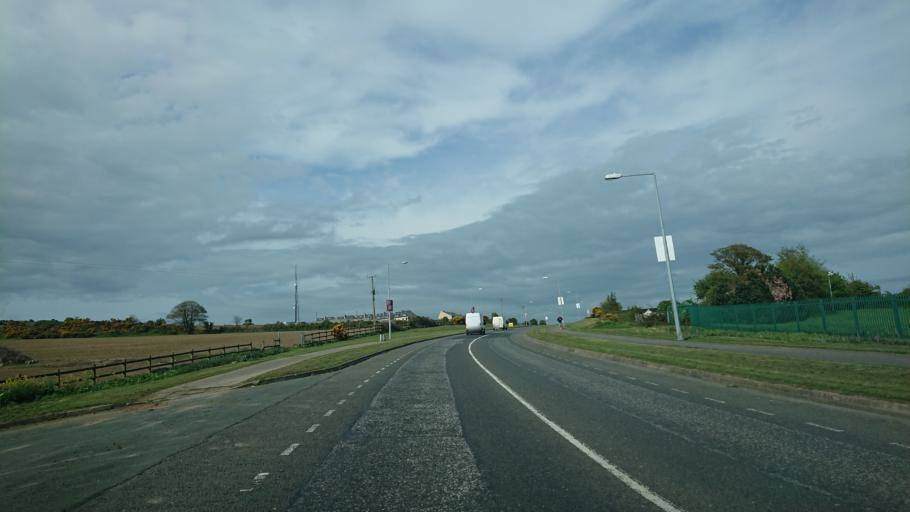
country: IE
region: Munster
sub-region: Waterford
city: Waterford
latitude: 52.2572
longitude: -7.1558
